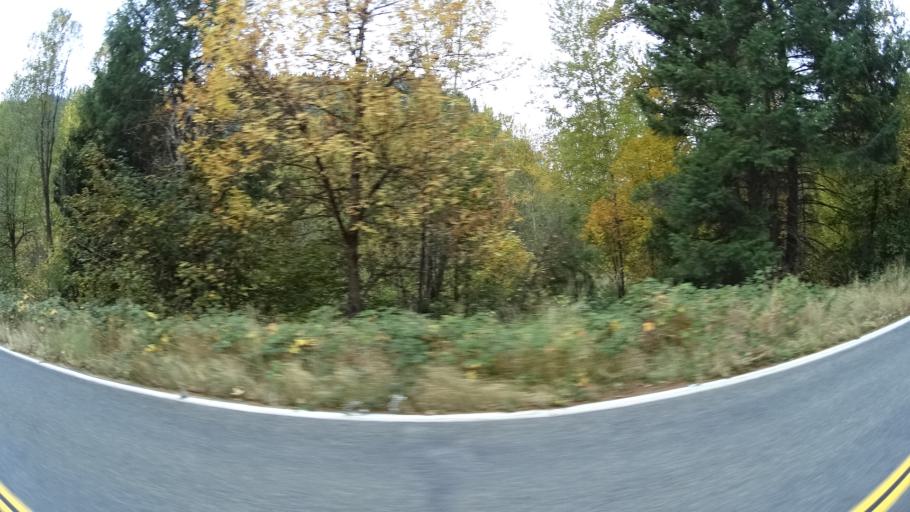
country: US
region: California
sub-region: Siskiyou County
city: Happy Camp
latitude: 41.8808
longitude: -123.4215
